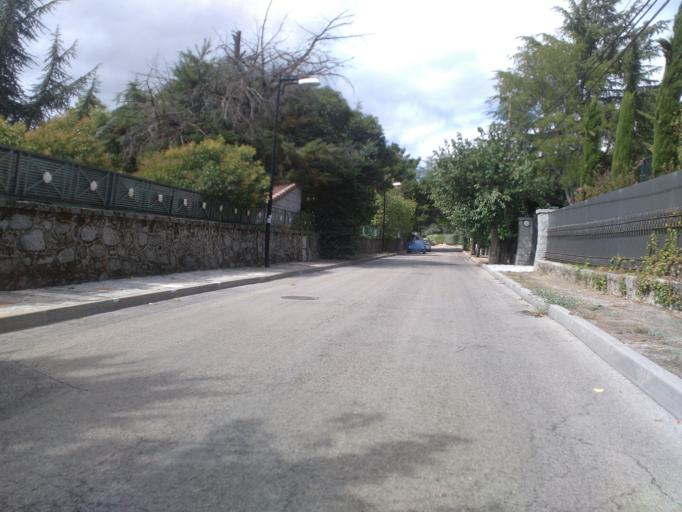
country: ES
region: Madrid
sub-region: Provincia de Madrid
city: Torrelodones
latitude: 40.5817
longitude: -3.9583
